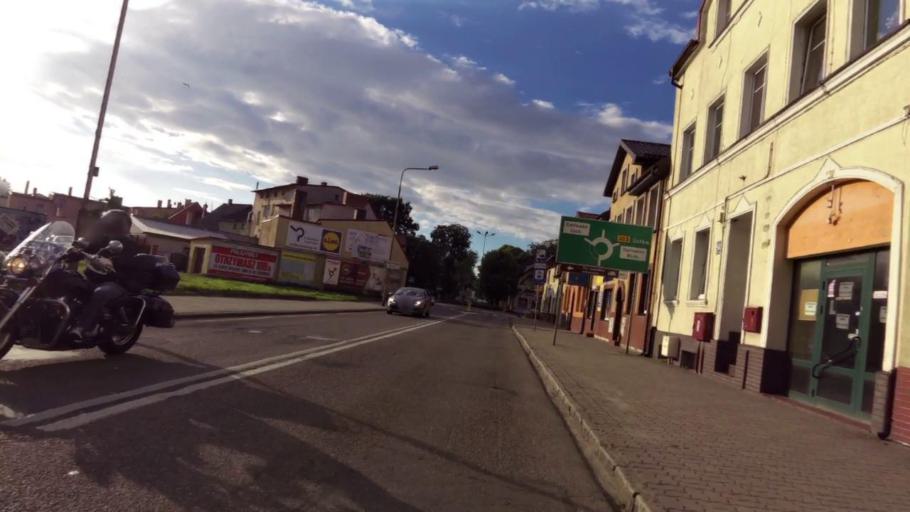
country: PL
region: West Pomeranian Voivodeship
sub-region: Powiat slawienski
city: Darlowo
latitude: 54.4169
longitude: 16.4103
